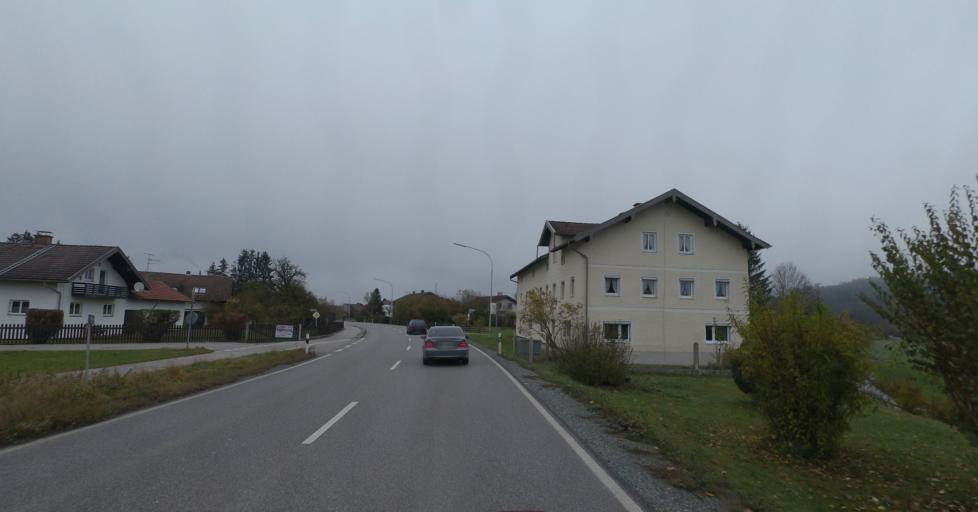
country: DE
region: Bavaria
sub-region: Upper Bavaria
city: Engelsberg
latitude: 48.1024
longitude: 12.5641
